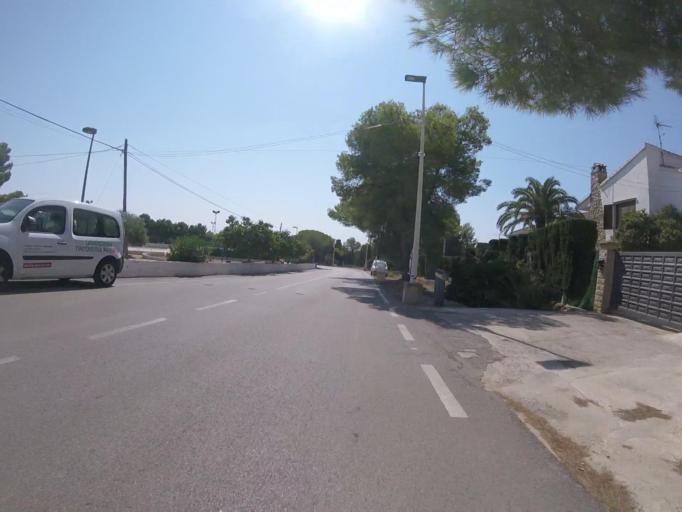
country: ES
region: Valencia
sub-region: Provincia de Castello
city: Alcoceber
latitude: 40.2506
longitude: 0.2818
